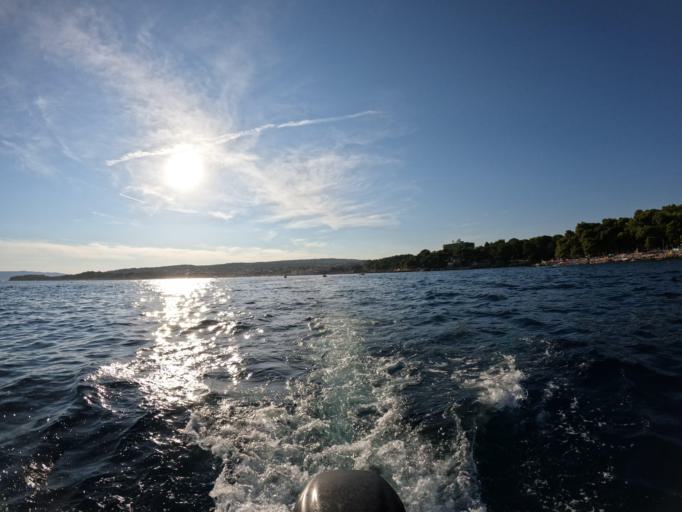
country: HR
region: Primorsko-Goranska
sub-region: Grad Krk
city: Krk
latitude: 45.0222
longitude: 14.5858
